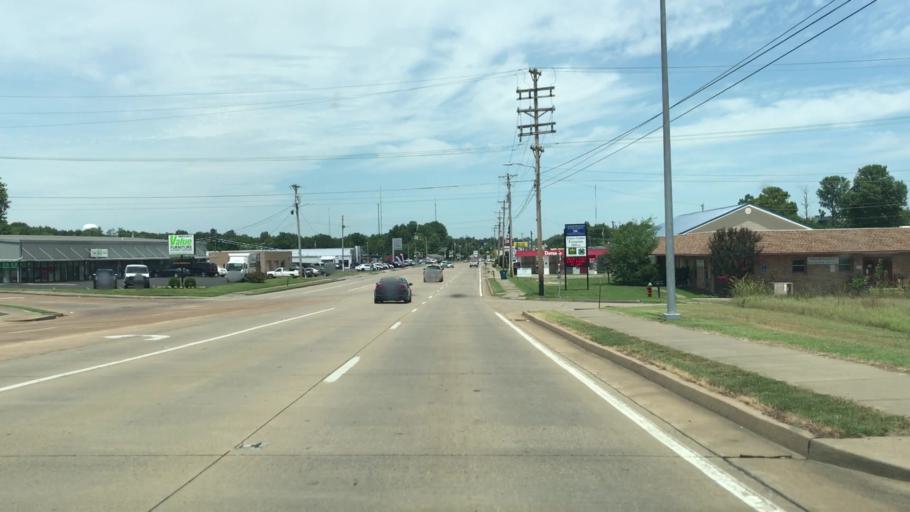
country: US
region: Kentucky
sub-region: Graves County
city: Mayfield
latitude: 36.7514
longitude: -88.6385
